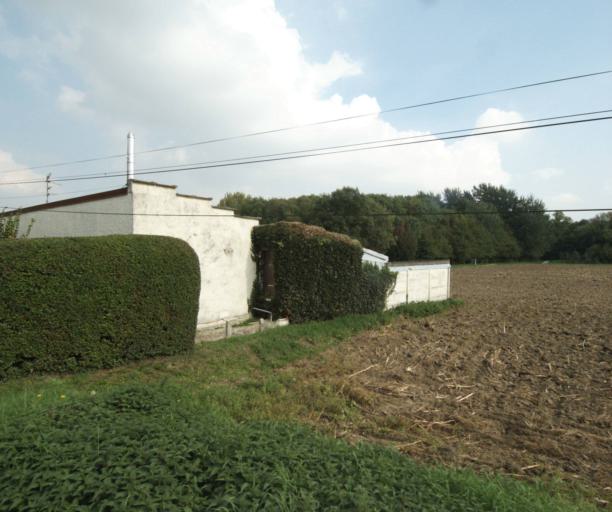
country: FR
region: Nord-Pas-de-Calais
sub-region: Departement du Nord
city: Santes
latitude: 50.5815
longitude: 2.9611
